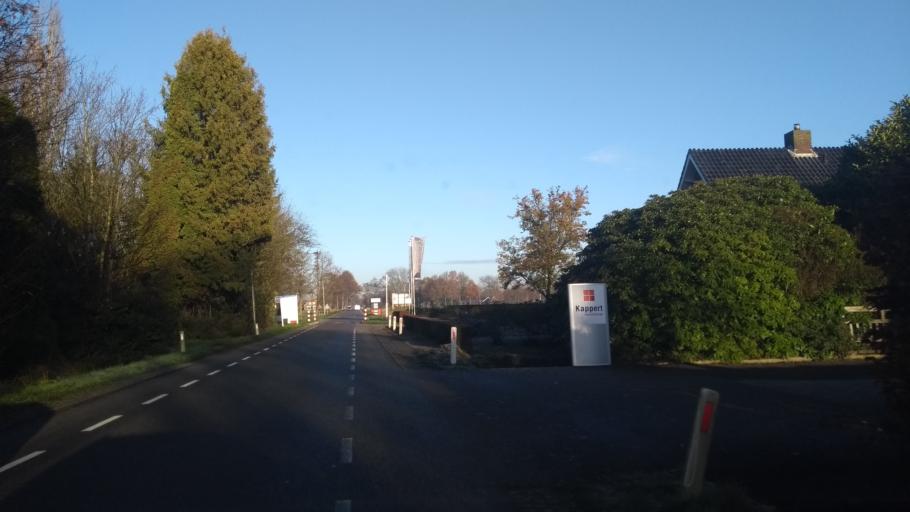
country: NL
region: Overijssel
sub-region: Gemeente Dalfsen
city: Dalfsen
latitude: 52.5954
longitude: 6.2846
